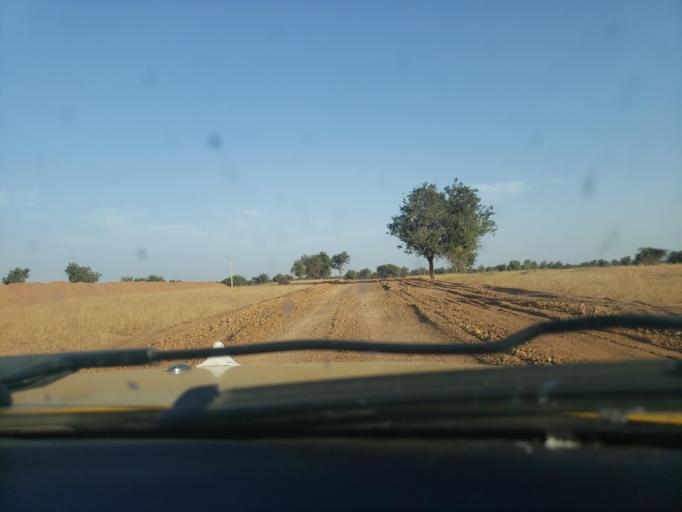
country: SN
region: Louga
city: Dara
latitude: 15.4269
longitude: -15.7420
